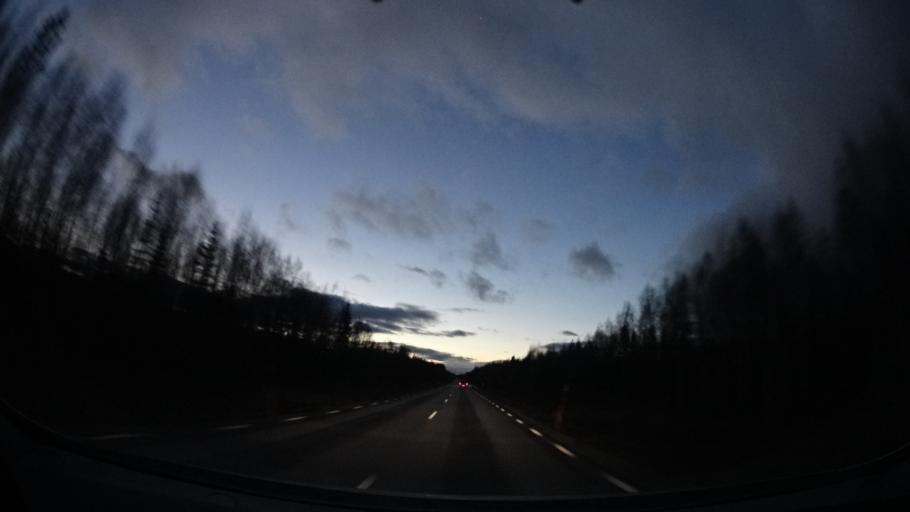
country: SE
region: Vaesterbotten
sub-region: Dorotea Kommun
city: Dorotea
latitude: 64.2500
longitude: 16.6003
